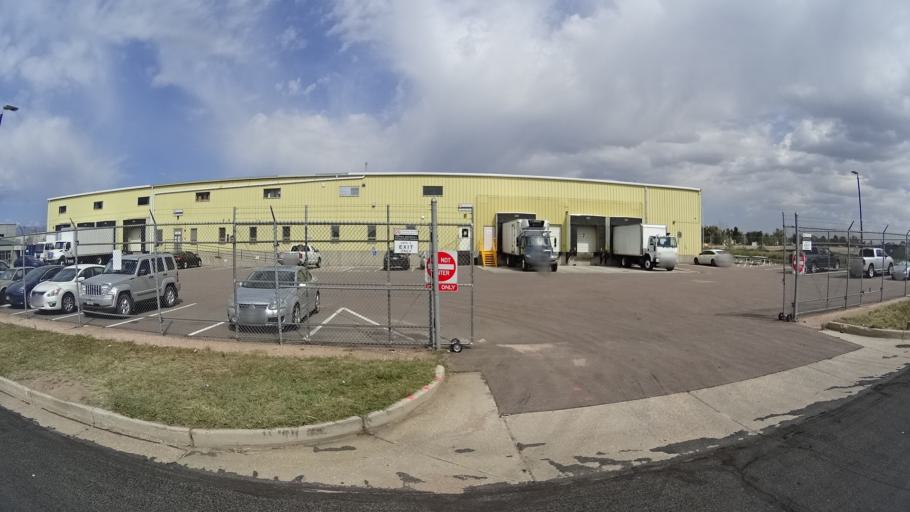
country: US
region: Colorado
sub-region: El Paso County
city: Cimarron Hills
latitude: 38.8441
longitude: -104.7299
